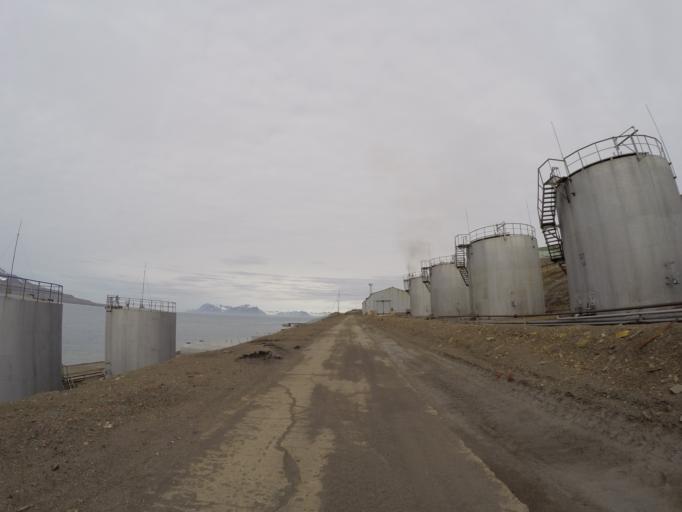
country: SJ
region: Svalbard
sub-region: Spitsbergen
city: Longyearbyen
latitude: 78.0517
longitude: 14.2128
